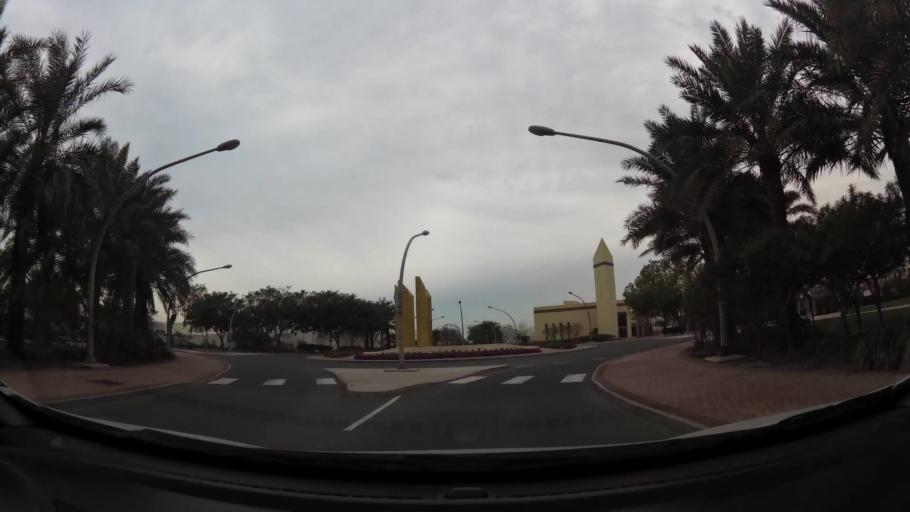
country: BH
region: Central Governorate
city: Dar Kulayb
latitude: 25.8336
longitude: 50.6145
